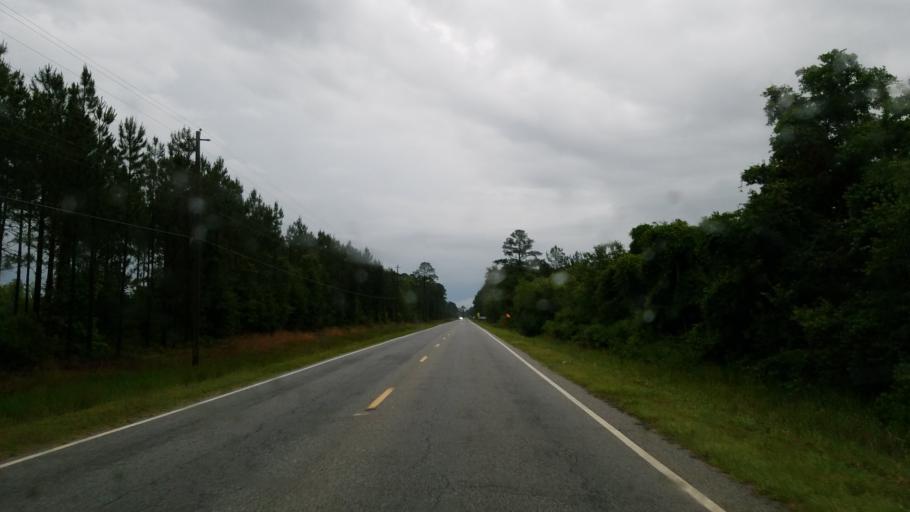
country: US
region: Georgia
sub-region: Lanier County
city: Lakeland
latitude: 31.0464
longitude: -83.1115
